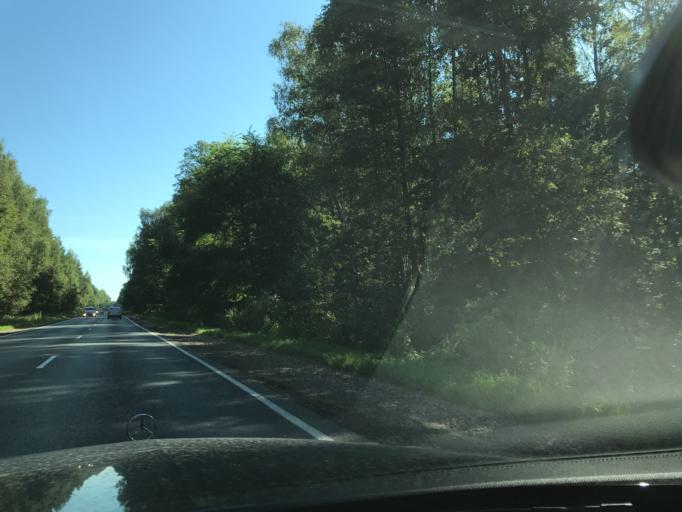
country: RU
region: Vladimir
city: Kirzhach
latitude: 56.1212
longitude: 38.7609
